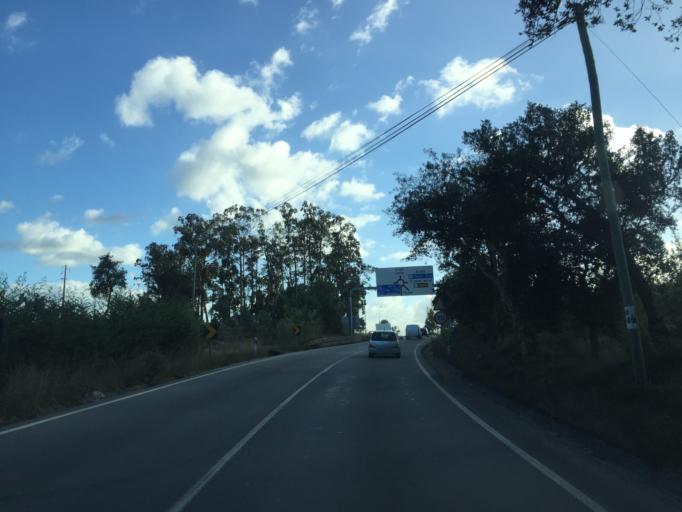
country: PT
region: Leiria
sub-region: Leiria
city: Souto da Carpalhosa
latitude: 39.8560
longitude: -8.8353
